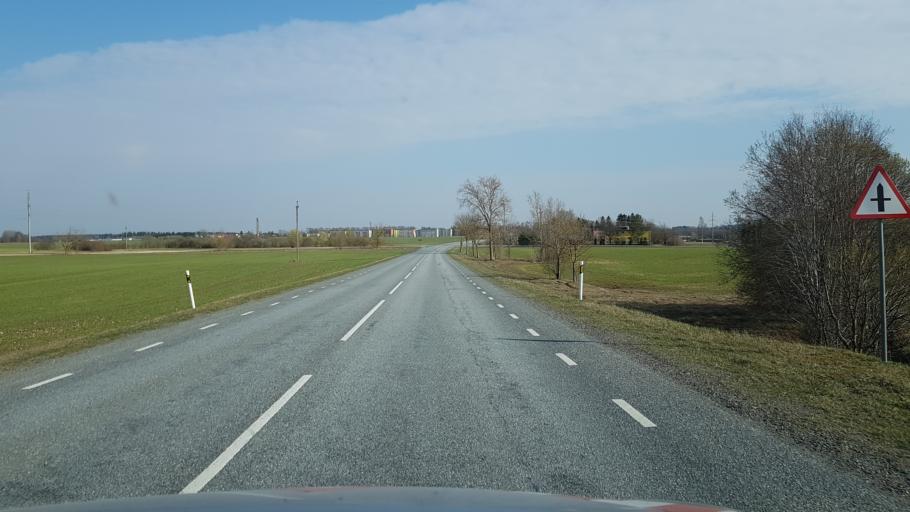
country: EE
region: Laeaene-Virumaa
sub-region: Kadrina vald
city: Kadrina
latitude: 59.3551
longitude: 26.1161
